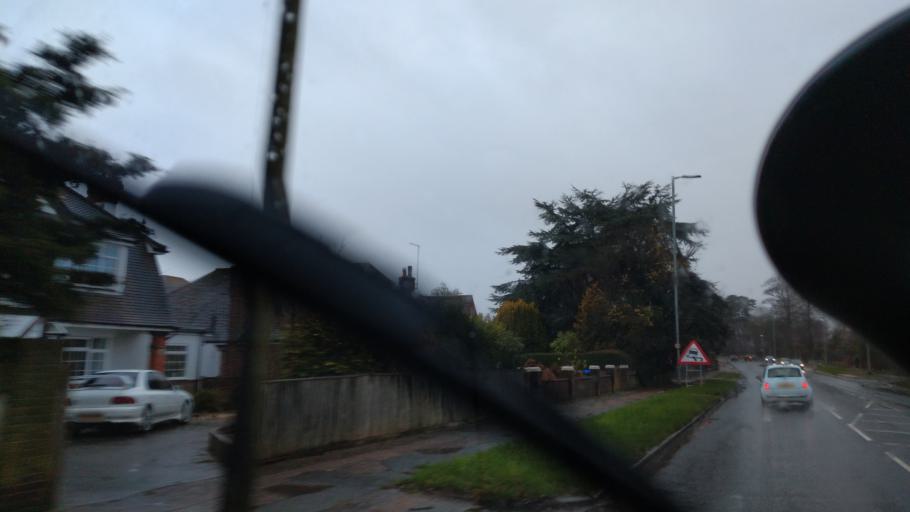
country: GB
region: England
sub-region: West Sussex
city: Broadwater
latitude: 50.8341
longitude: -0.3691
